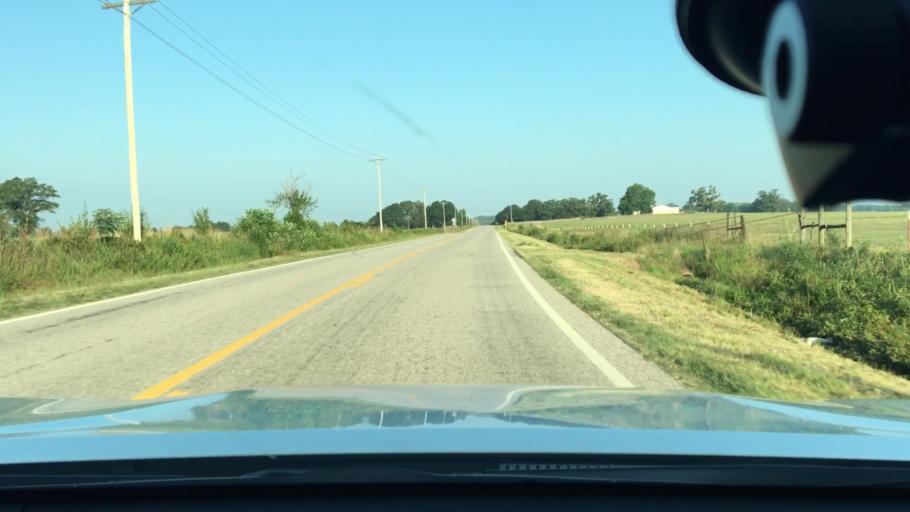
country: US
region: Arkansas
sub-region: Johnson County
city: Coal Hill
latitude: 35.3506
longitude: -93.5684
